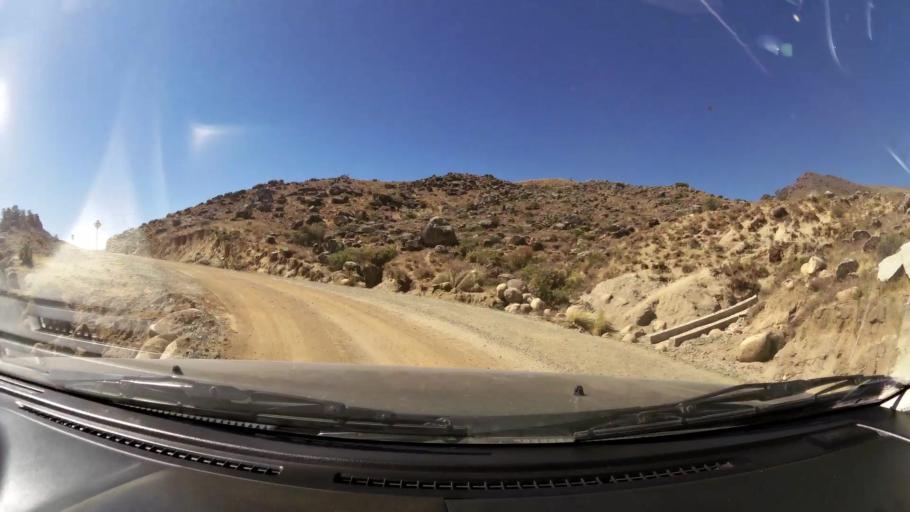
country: PE
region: Huancavelica
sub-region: Huaytara
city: Quito-Arma
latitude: -13.6284
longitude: -75.3567
